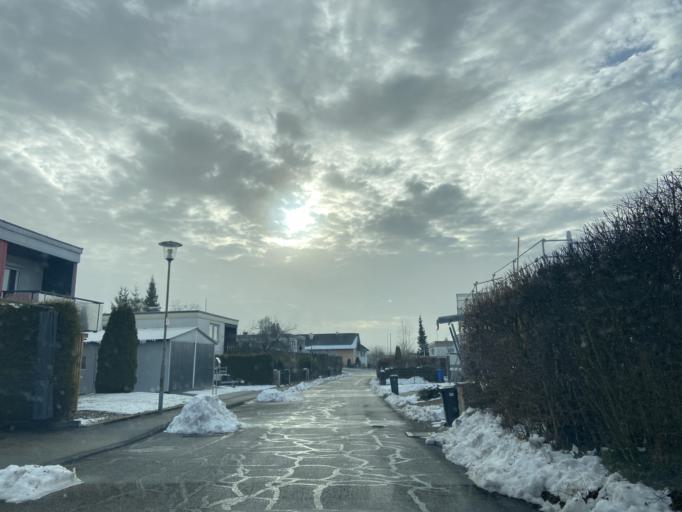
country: DE
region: Baden-Wuerttemberg
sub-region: Tuebingen Region
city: Gammertingen
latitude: 48.2519
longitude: 9.2253
